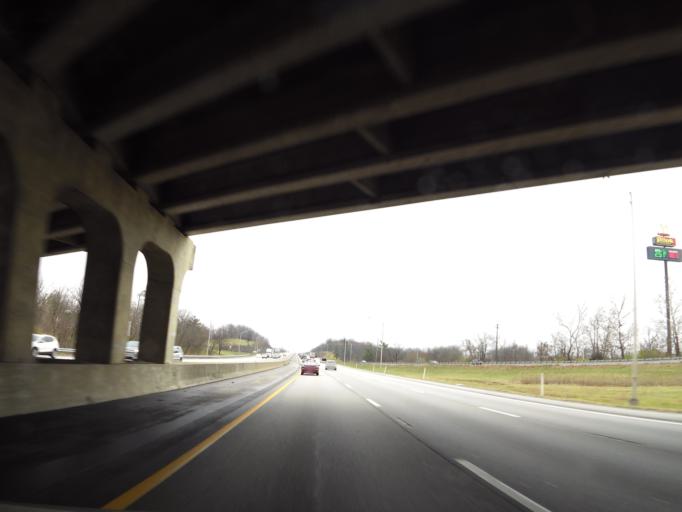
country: US
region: Kentucky
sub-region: Scott County
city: Georgetown
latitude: 38.2765
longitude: -84.5577
